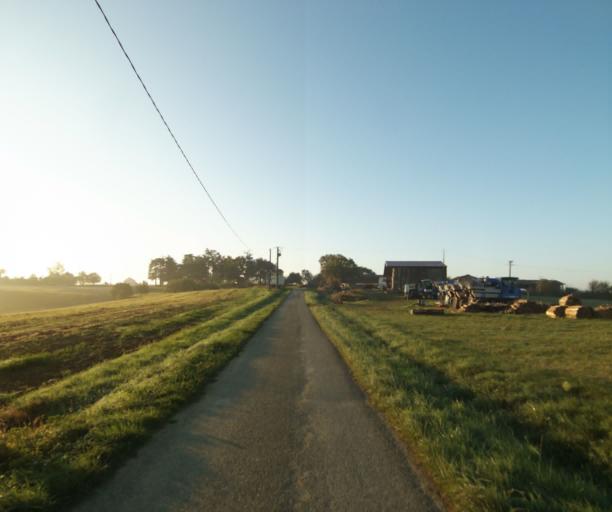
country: FR
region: Midi-Pyrenees
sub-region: Departement du Gers
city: Vic-Fezensac
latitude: 43.7698
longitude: 0.1928
